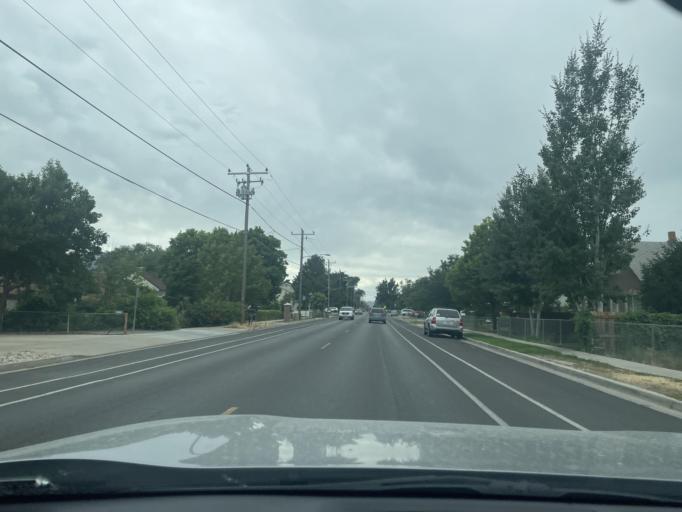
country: US
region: Utah
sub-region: Salt Lake County
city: Millcreek
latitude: 40.6941
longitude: -111.8770
